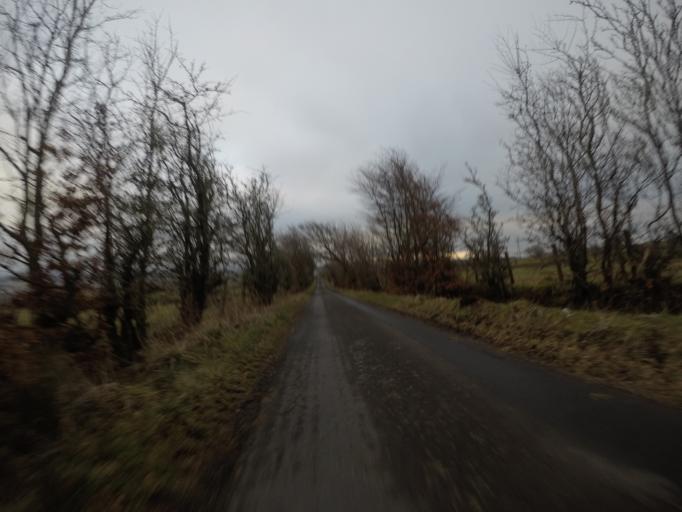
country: GB
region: Scotland
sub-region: North Ayrshire
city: Dalry
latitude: 55.7243
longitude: -4.7632
